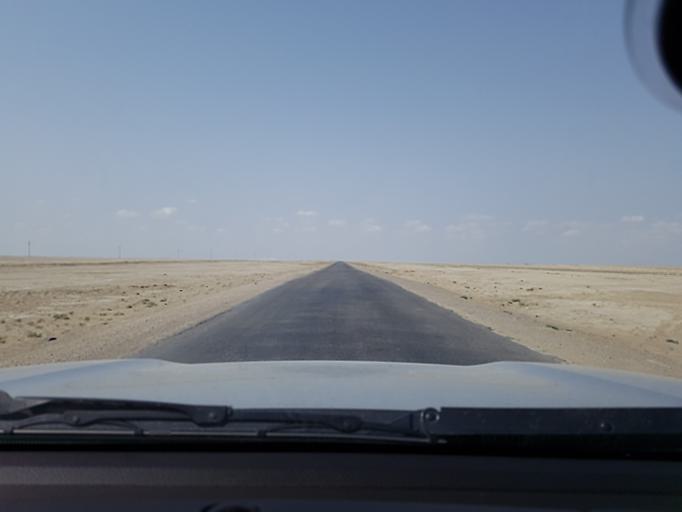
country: TM
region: Balkan
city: Gumdag
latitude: 38.6664
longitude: 54.4012
